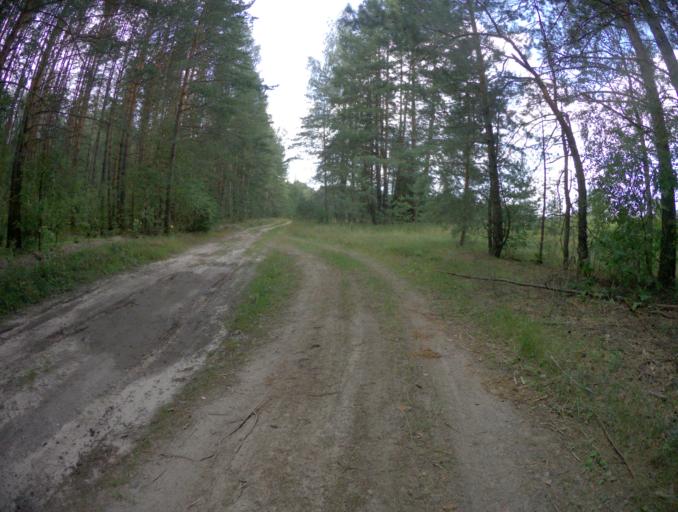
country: RU
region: Vladimir
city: Vorsha
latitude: 55.9667
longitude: 40.1804
